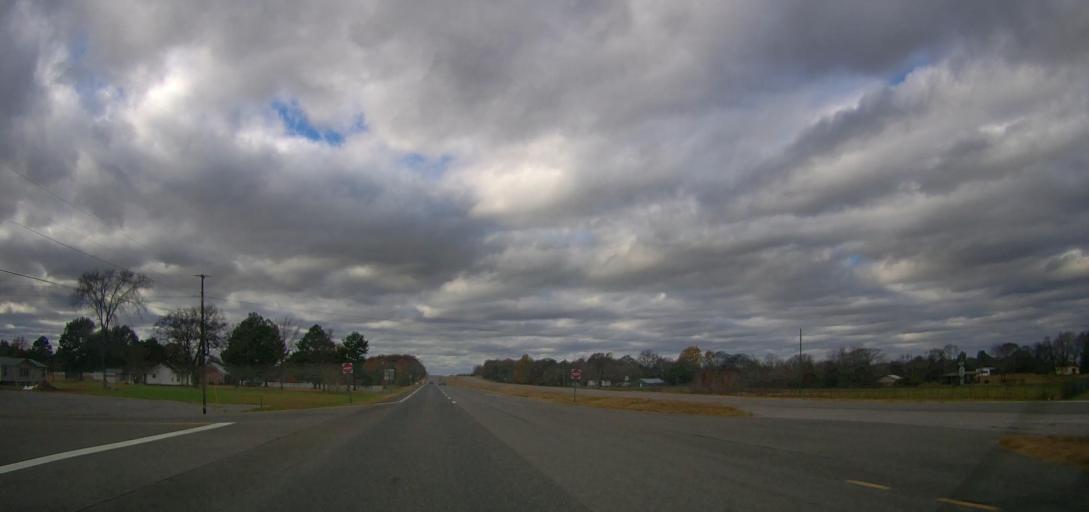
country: US
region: Alabama
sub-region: Morgan County
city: Danville
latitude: 34.4097
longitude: -87.1490
